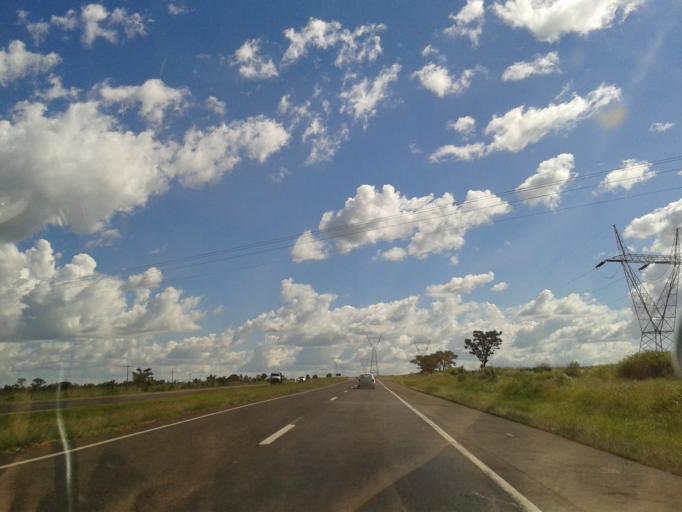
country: BR
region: Goias
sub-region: Goiatuba
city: Goiatuba
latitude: -17.8858
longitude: -49.2323
